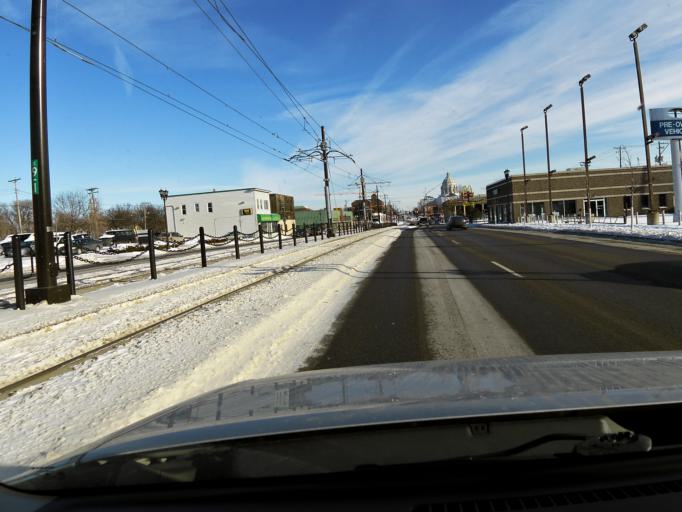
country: US
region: Minnesota
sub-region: Ramsey County
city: Saint Paul
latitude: 44.9557
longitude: -93.1122
